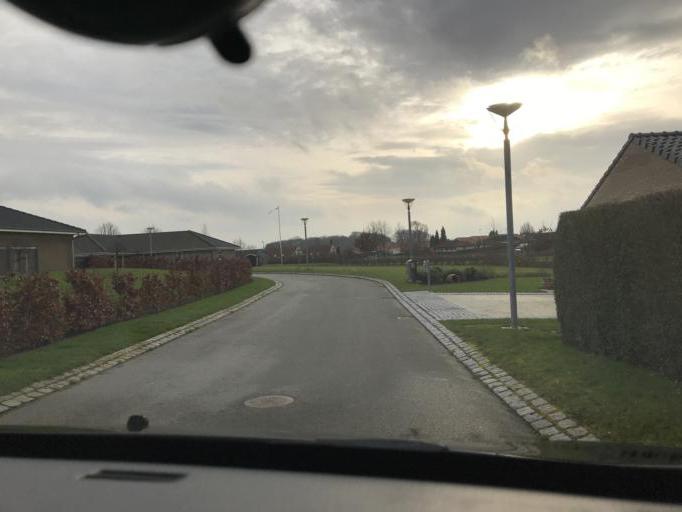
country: DK
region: South Denmark
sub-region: Faaborg-Midtfyn Kommune
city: Ringe
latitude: 55.2477
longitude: 10.4598
